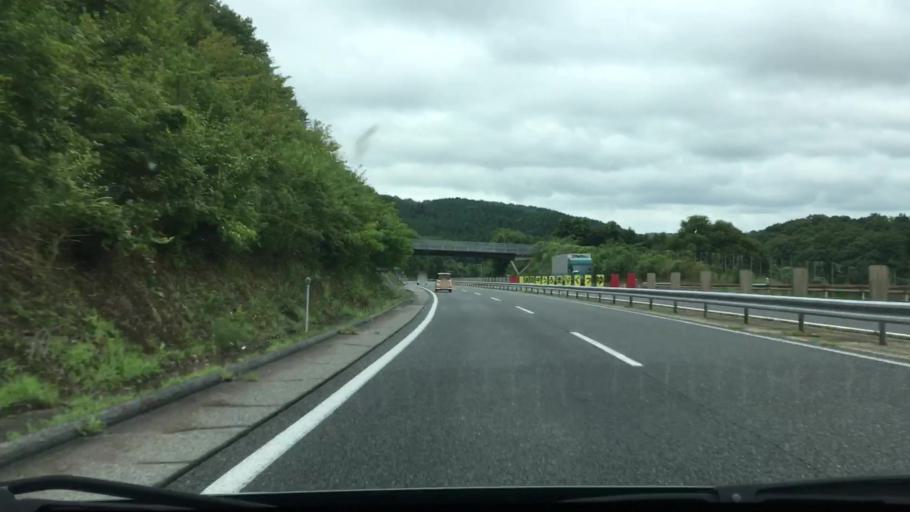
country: JP
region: Hiroshima
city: Miyoshi
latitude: 34.7767
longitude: 132.8386
